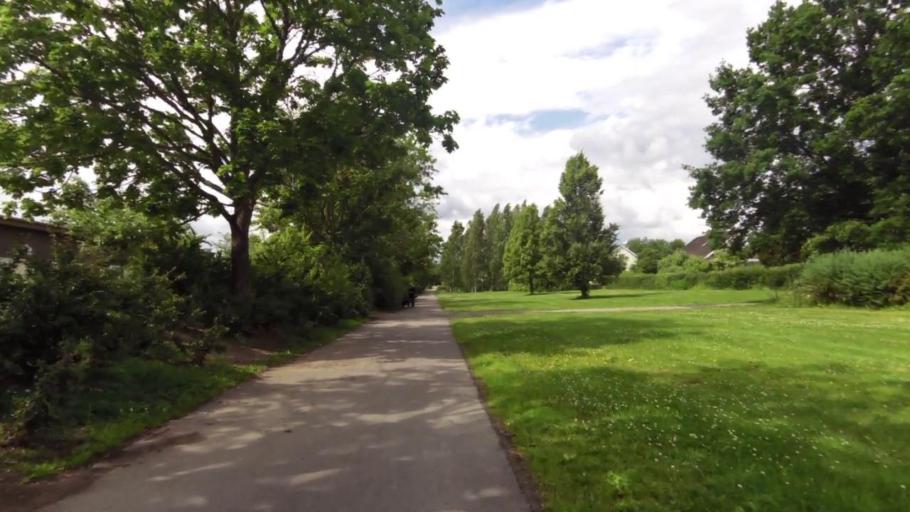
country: SE
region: OEstergoetland
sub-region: Linkopings Kommun
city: Malmslatt
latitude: 58.4156
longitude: 15.5637
